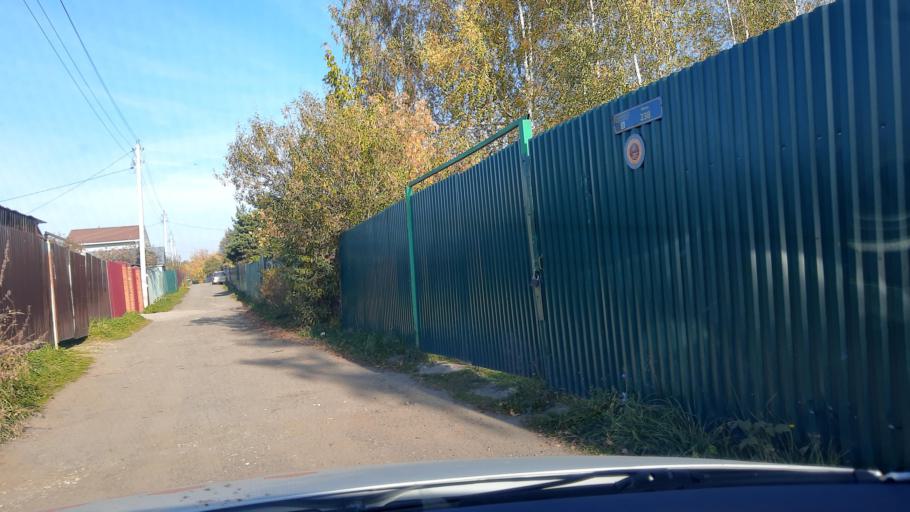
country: RU
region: Moskovskaya
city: Imeni Vorovskogo
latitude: 55.7821
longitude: 38.3642
